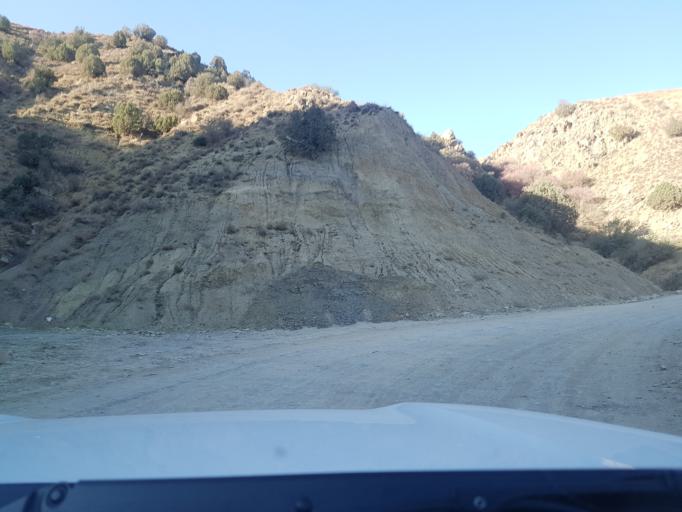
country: TM
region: Ahal
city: Baharly
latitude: 38.4416
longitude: 57.0482
